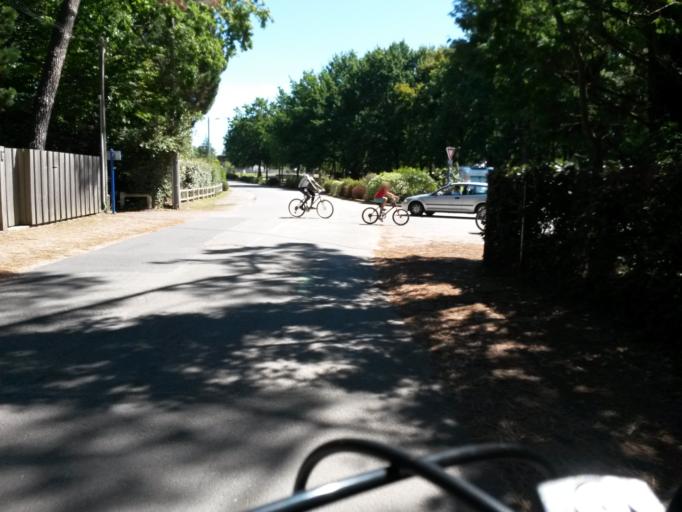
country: FR
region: Pays de la Loire
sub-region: Departement de la Loire-Atlantique
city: Mesquer
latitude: 47.4057
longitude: -2.4876
